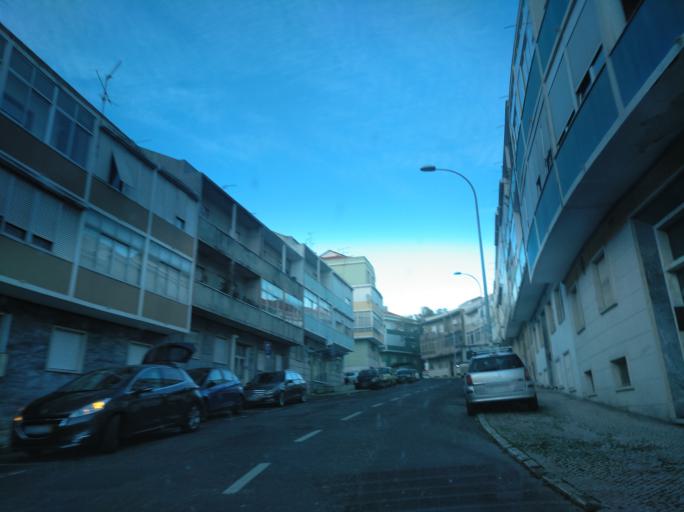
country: PT
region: Lisbon
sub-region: Amadora
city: Amadora
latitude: 38.7461
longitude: -9.2227
